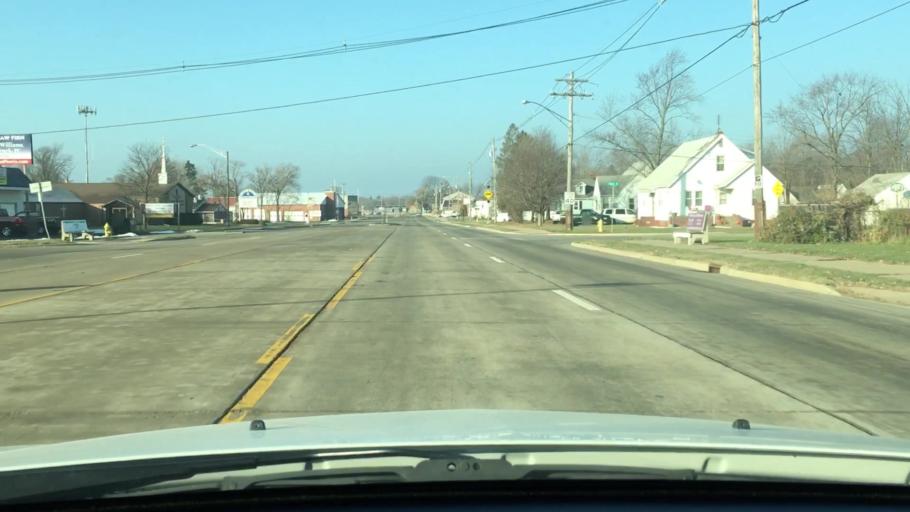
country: US
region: Illinois
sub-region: Woodford County
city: Germantown Hills
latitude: 40.6912
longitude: -89.4960
